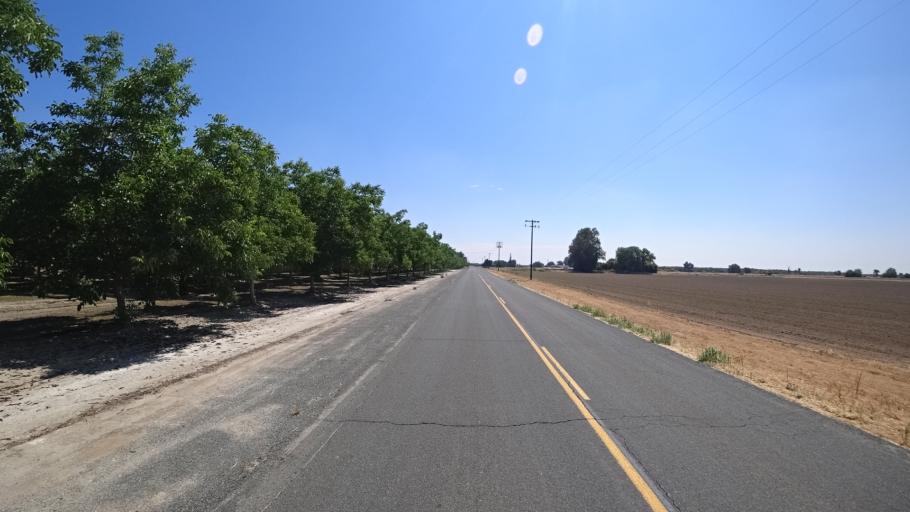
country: US
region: California
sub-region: Fresno County
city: Laton
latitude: 36.4308
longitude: -119.6273
